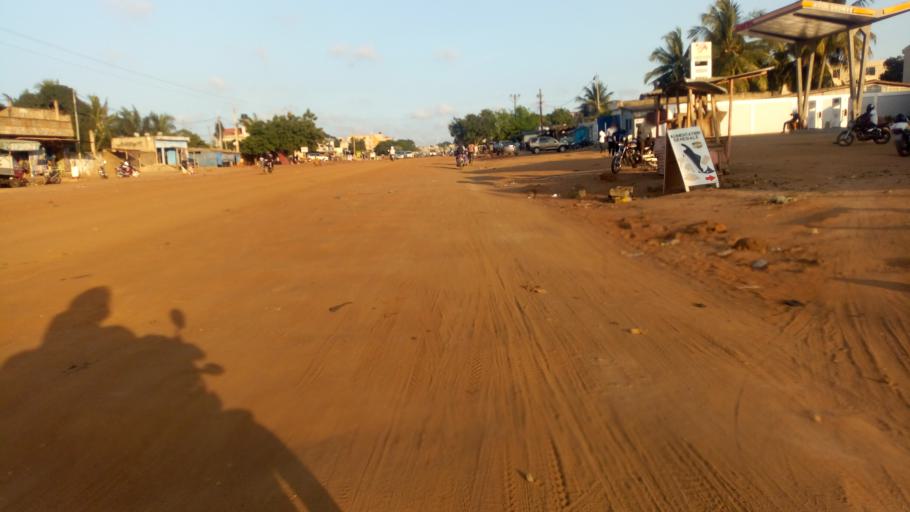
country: TG
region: Maritime
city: Lome
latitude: 6.2173
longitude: 1.1833
